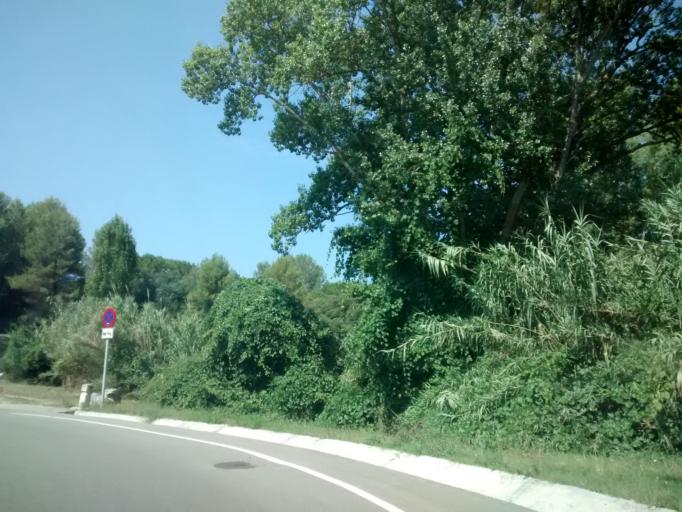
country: ES
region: Catalonia
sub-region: Provincia de Barcelona
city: Barbera del Valles
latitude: 41.5054
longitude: 2.1003
